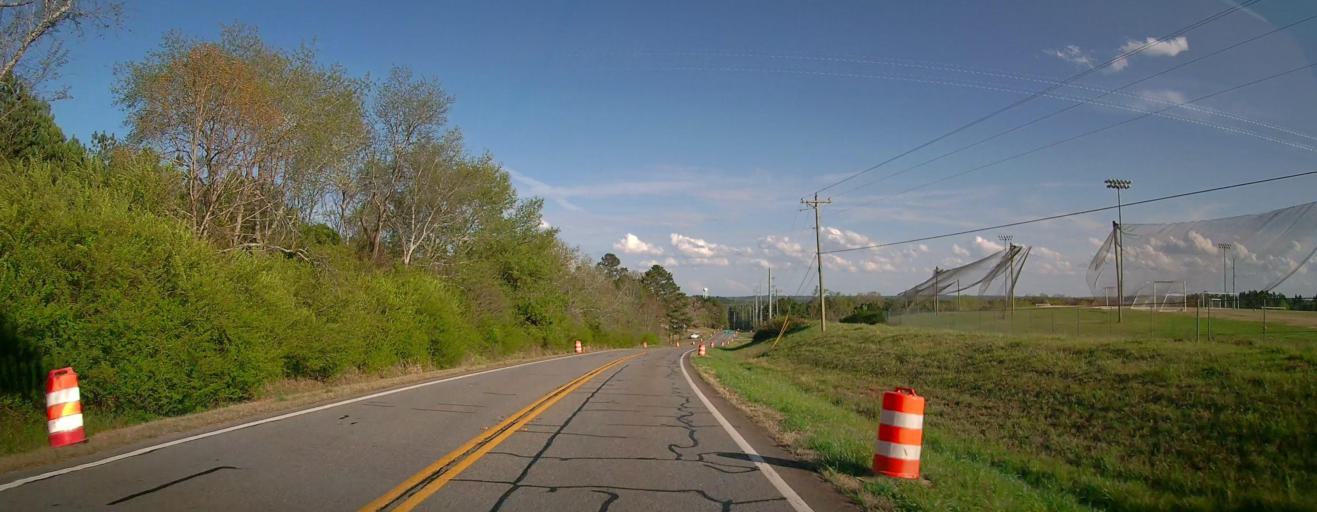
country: US
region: Georgia
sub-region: Baldwin County
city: Milledgeville
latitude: 33.1070
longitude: -83.2792
